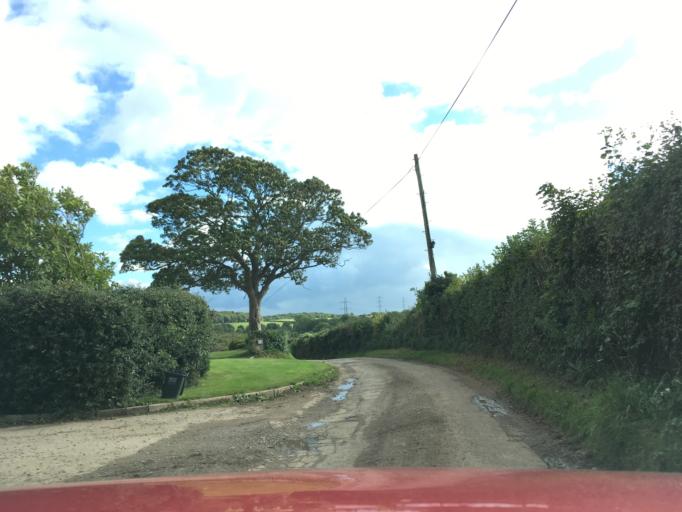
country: GB
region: England
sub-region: South Gloucestershire
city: Falfield
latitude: 51.6172
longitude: -2.4697
